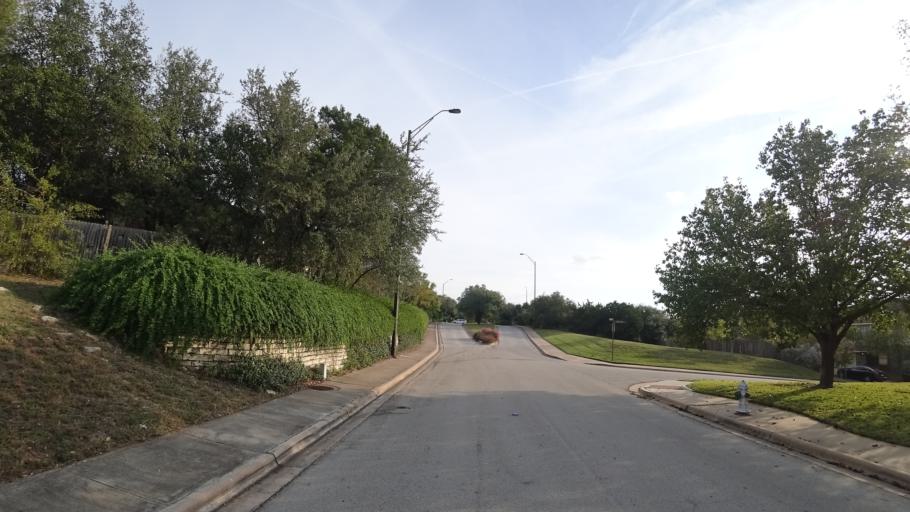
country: US
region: Texas
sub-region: Travis County
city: Hudson Bend
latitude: 30.3775
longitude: -97.8881
